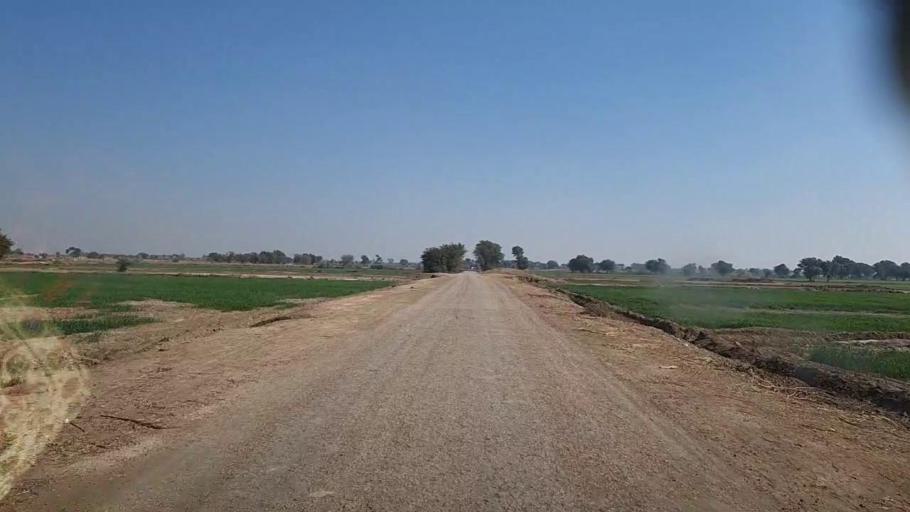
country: PK
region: Sindh
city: Khairpur
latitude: 27.9780
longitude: 69.8453
